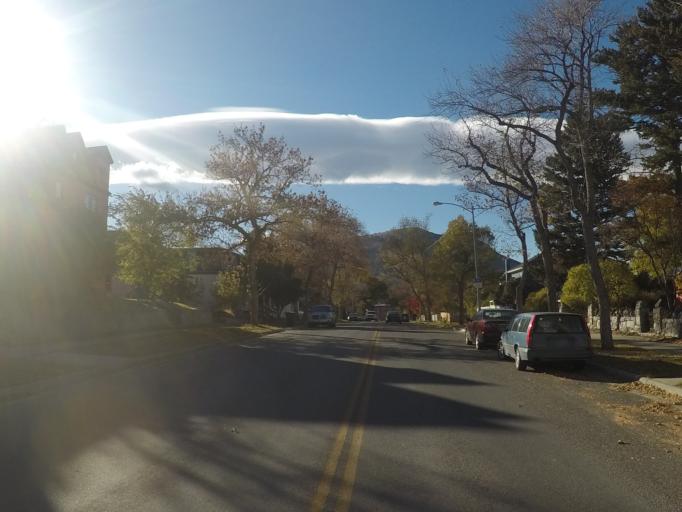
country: US
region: Montana
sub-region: Lewis and Clark County
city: Helena
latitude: 46.5867
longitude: -112.0288
